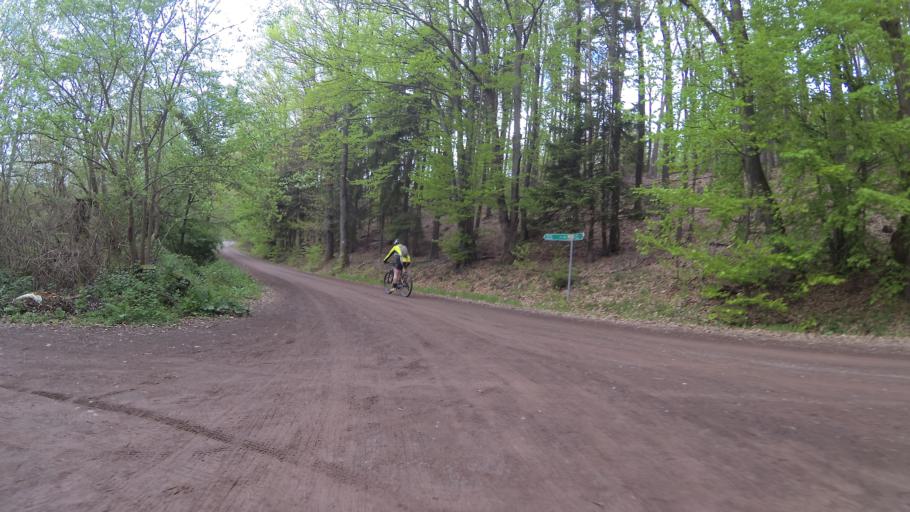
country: DE
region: Saarland
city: Schmelz
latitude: 49.4266
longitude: 6.8582
